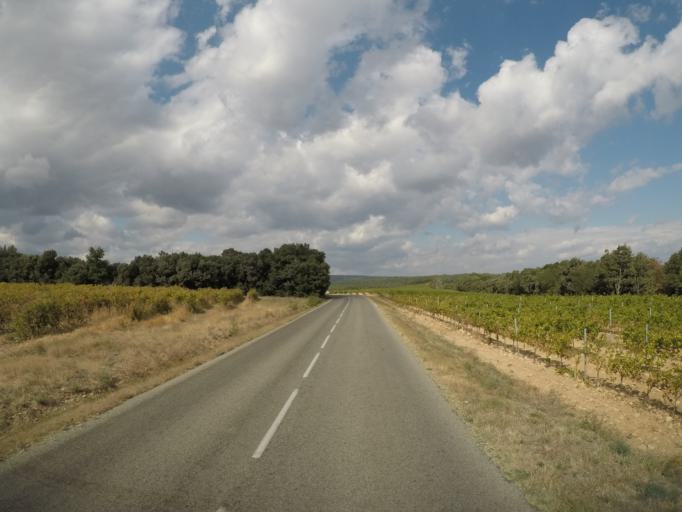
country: FR
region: Rhone-Alpes
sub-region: Departement de la Drome
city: Suze-la-Rousse
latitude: 44.3194
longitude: 4.8256
